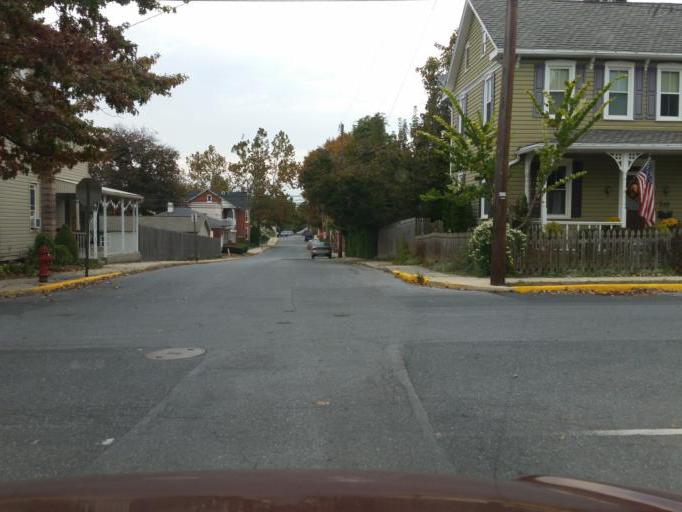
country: US
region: Pennsylvania
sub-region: Dauphin County
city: Hummelstown
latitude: 40.2636
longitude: -76.7148
